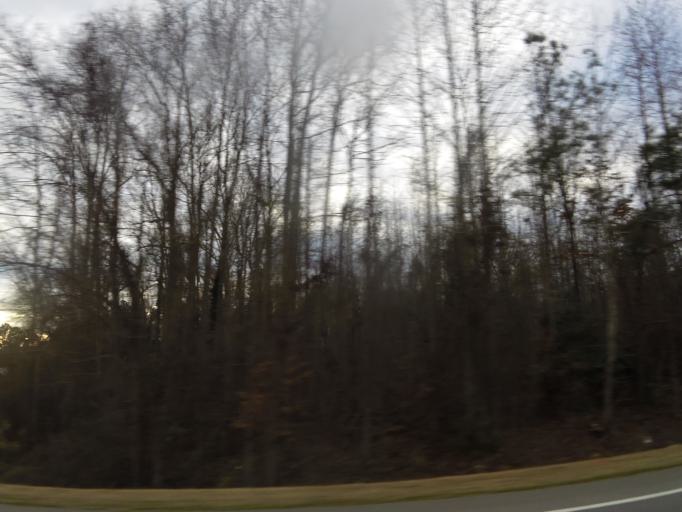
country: US
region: North Carolina
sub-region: Nash County
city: Rocky Mount
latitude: 35.9373
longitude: -77.8298
